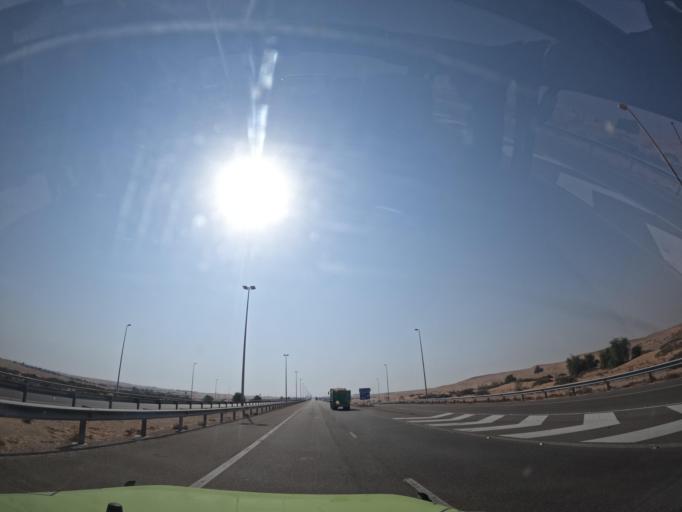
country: OM
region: Al Buraimi
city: Al Buraymi
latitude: 24.5129
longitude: 55.5639
